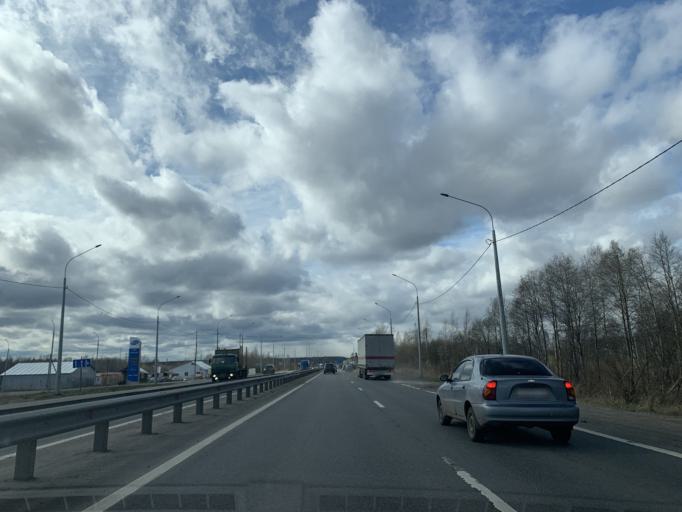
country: RU
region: Jaroslavl
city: Yaroslavl
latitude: 57.6821
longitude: 39.9176
